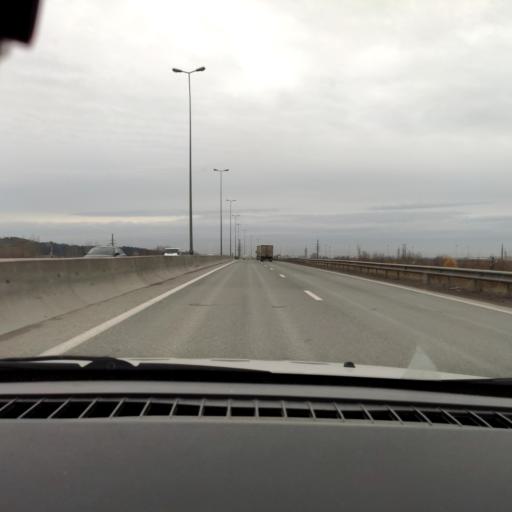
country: RU
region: Perm
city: Kondratovo
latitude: 57.9411
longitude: 56.1471
